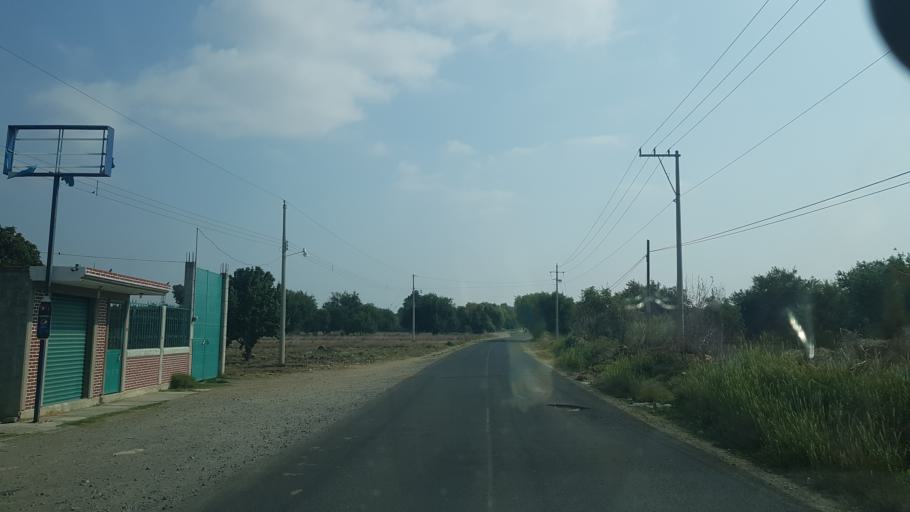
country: MX
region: Puebla
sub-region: Huejotzingo
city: San Juan Pancoac
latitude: 19.1268
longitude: -98.4205
